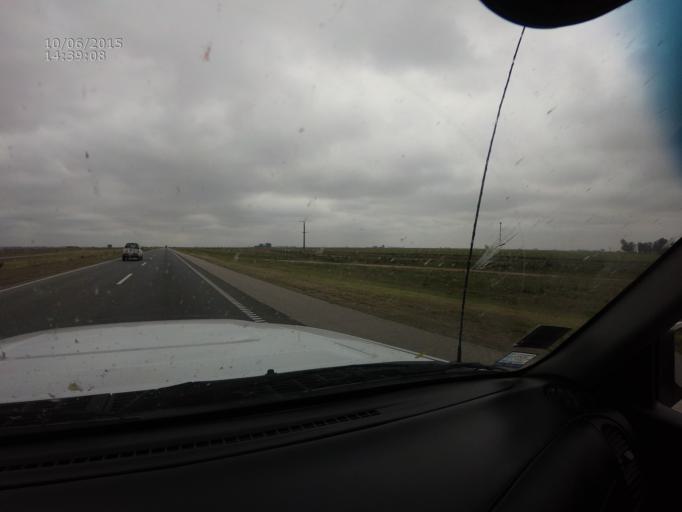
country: AR
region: Cordoba
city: James Craik
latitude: -32.0819
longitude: -63.4832
